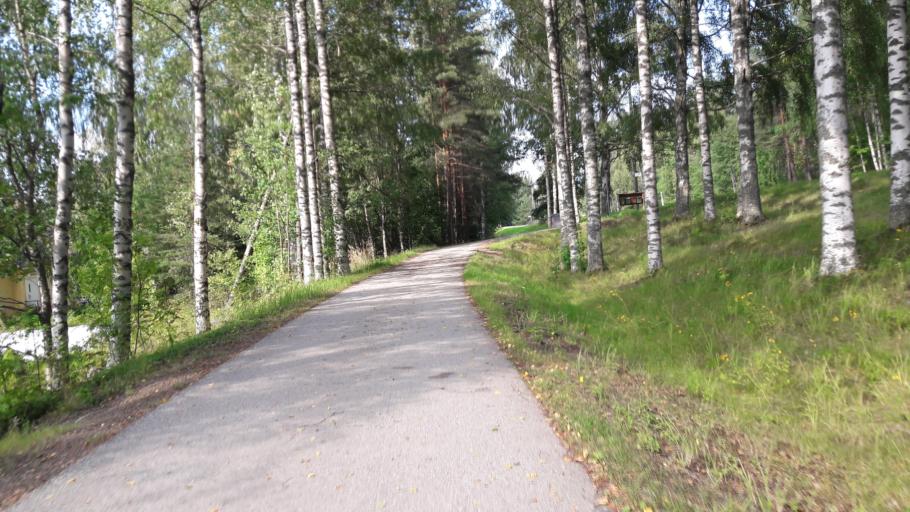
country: FI
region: North Karelia
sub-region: Joensuu
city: Joensuu
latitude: 62.5203
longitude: 29.8643
